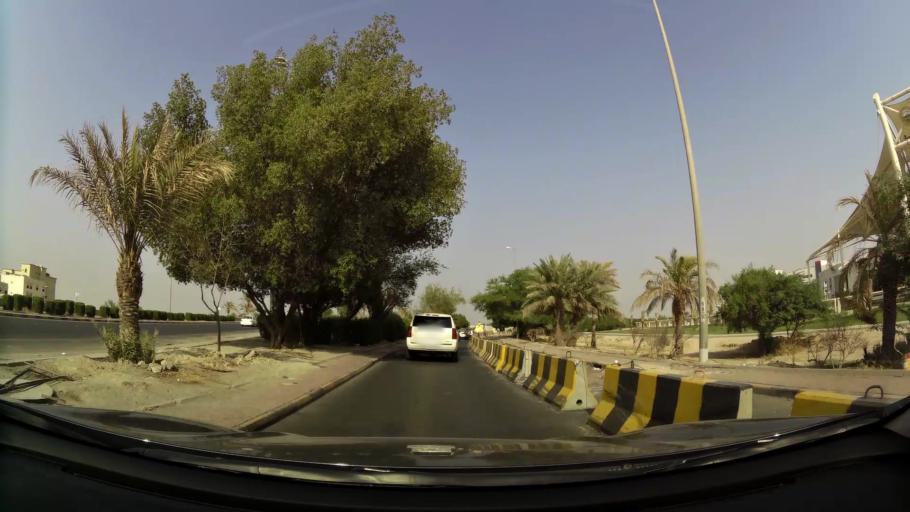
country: KW
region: Muhafazat al Jahra'
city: Al Jahra'
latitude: 29.3383
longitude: 47.7116
